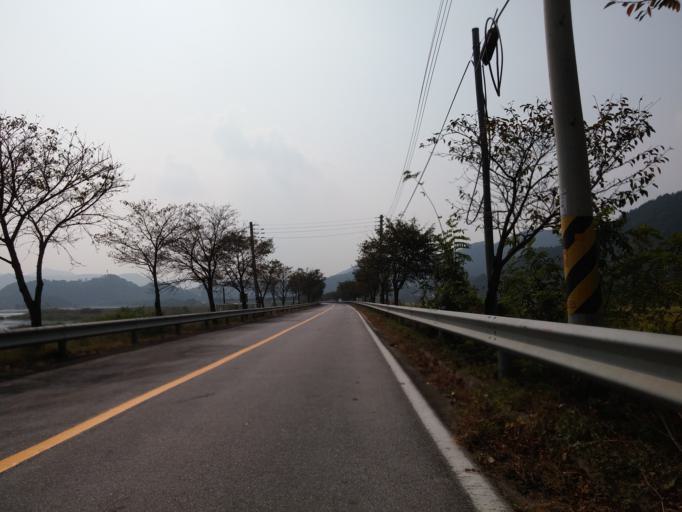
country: KR
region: Chungcheongbuk-do
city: Yong-dong
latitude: 36.3360
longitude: 127.7724
